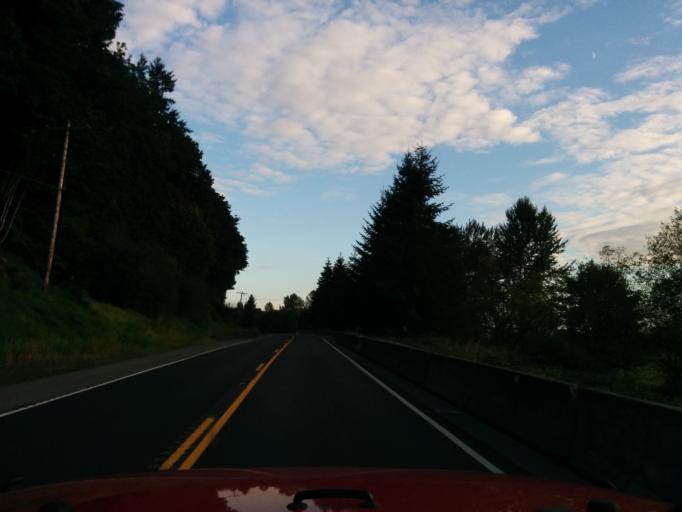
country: US
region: Washington
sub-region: Snohomish County
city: Monroe
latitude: 47.8012
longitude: -121.9794
